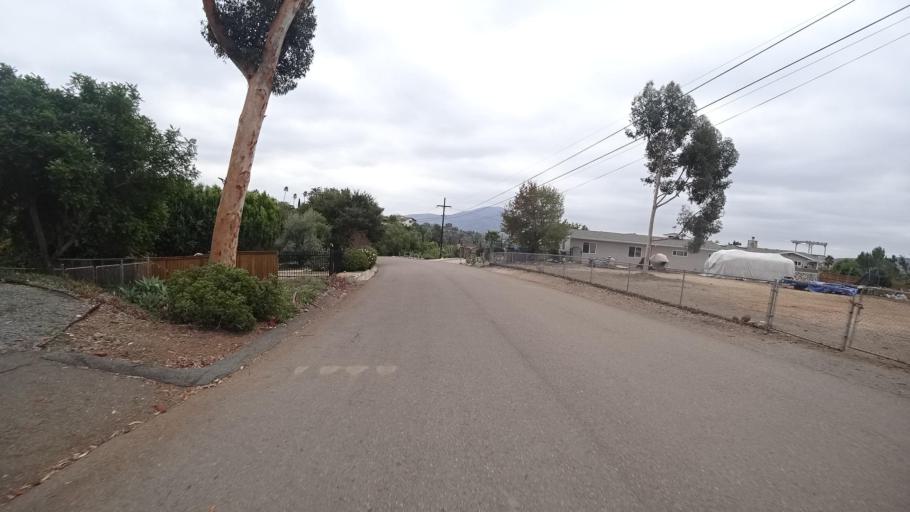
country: US
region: California
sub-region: San Diego County
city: Casa de Oro-Mount Helix
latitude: 32.7570
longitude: -116.9768
